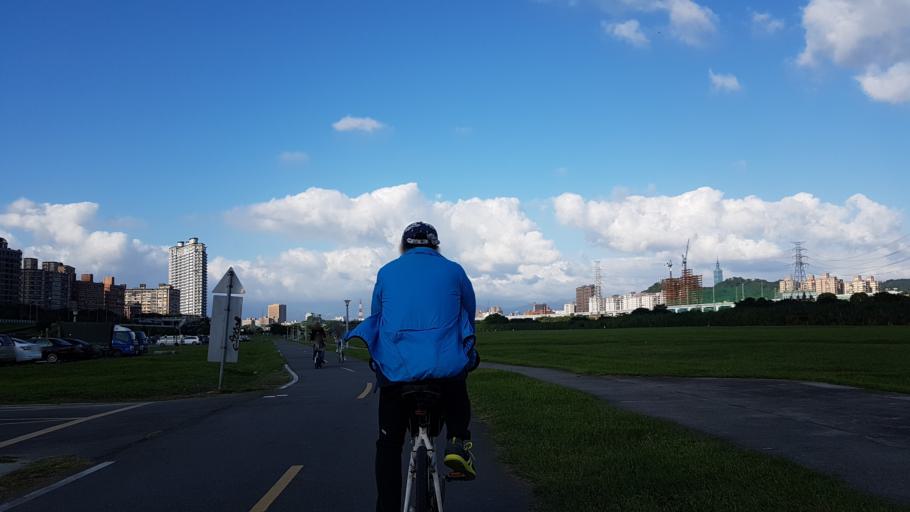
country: TW
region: Taipei
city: Taipei
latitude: 24.9921
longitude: 121.5290
